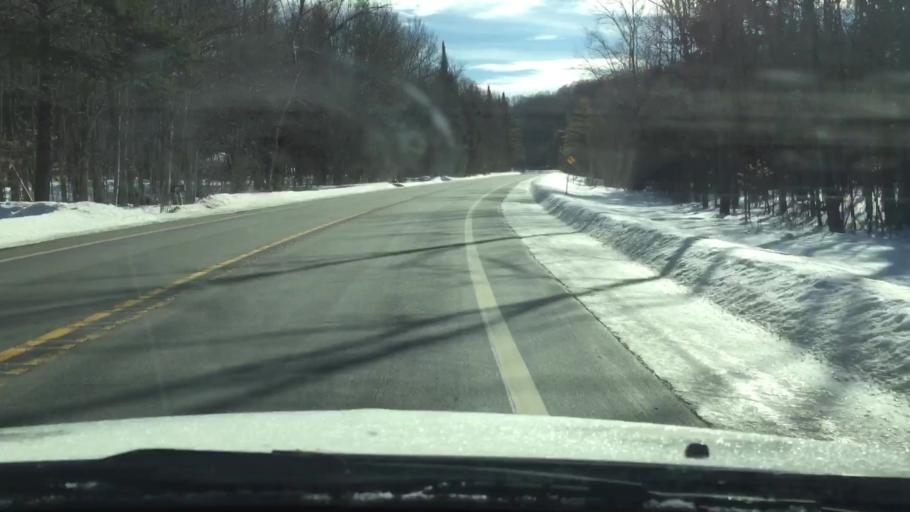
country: US
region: Michigan
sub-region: Antrim County
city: Mancelona
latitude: 45.0044
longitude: -85.0628
